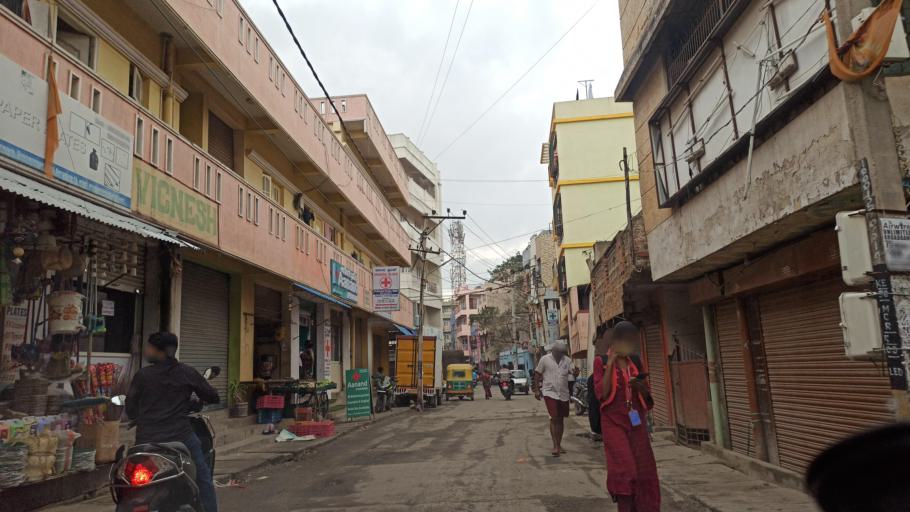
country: IN
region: Karnataka
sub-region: Bangalore Urban
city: Bangalore
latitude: 12.9951
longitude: 77.6753
